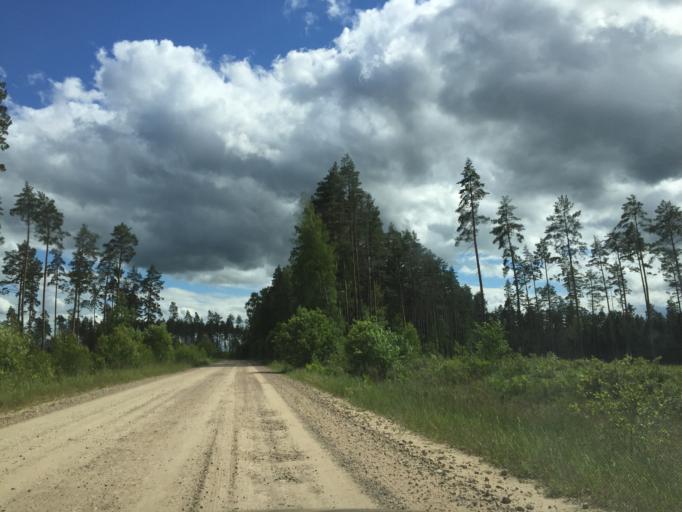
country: LV
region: Vecumnieki
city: Vecumnieki
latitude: 56.4893
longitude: 24.4077
